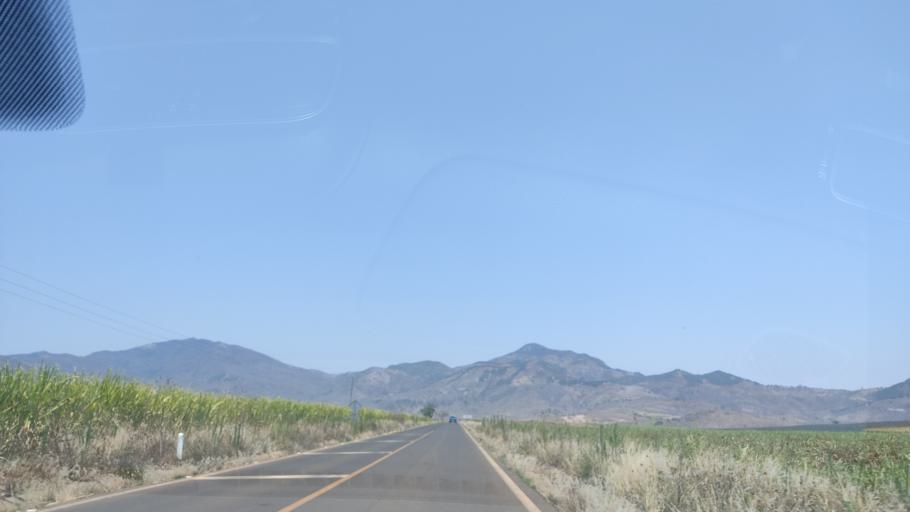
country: MX
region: Nayarit
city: Puga
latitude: 21.5926
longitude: -104.7412
